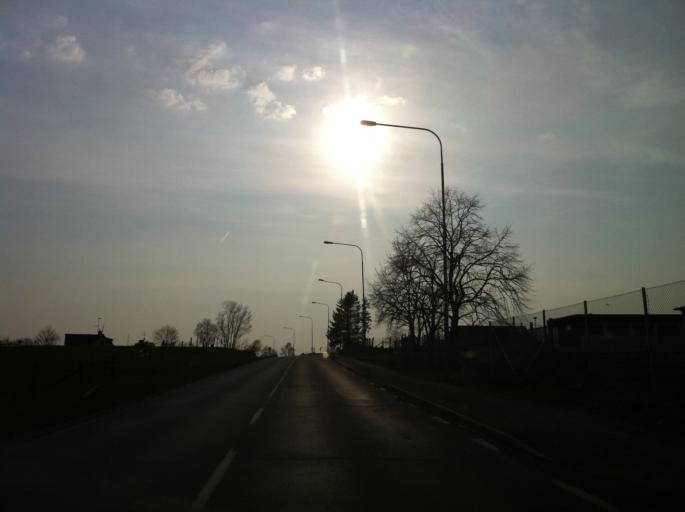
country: SE
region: Skane
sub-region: Svalovs Kommun
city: Svaloev
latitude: 55.9136
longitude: 13.1479
